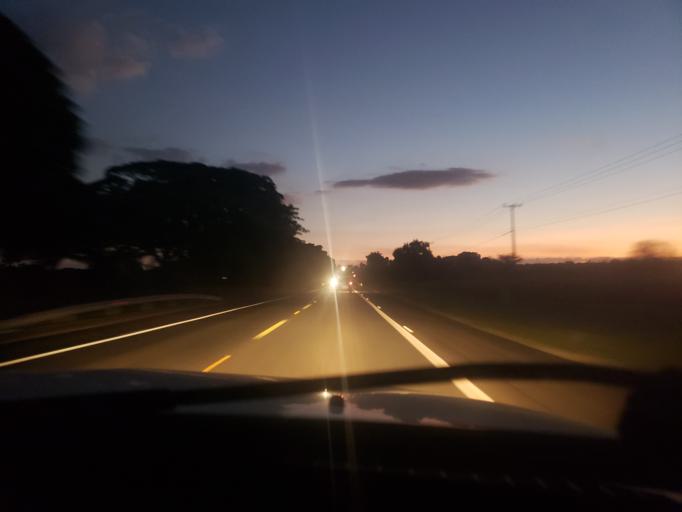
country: BR
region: Sao Paulo
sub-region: Conchal
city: Conchal
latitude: -22.3232
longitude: -47.1420
